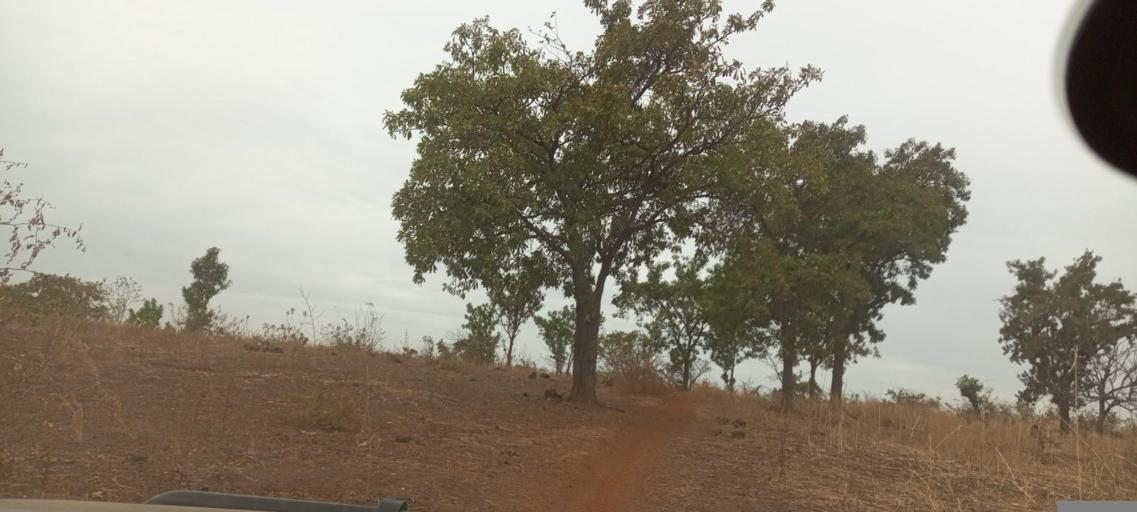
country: ML
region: Koulikoro
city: Kati
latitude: 12.8261
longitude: -8.4579
